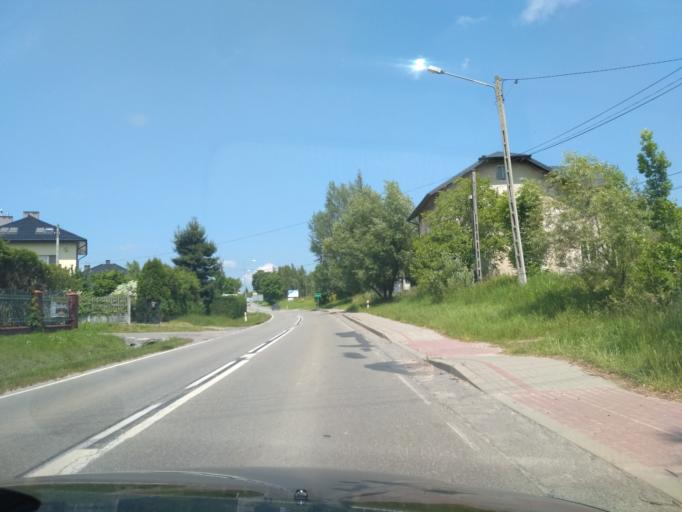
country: PL
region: Subcarpathian Voivodeship
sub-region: Powiat lancucki
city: Lancut
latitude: 50.0486
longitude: 22.2260
